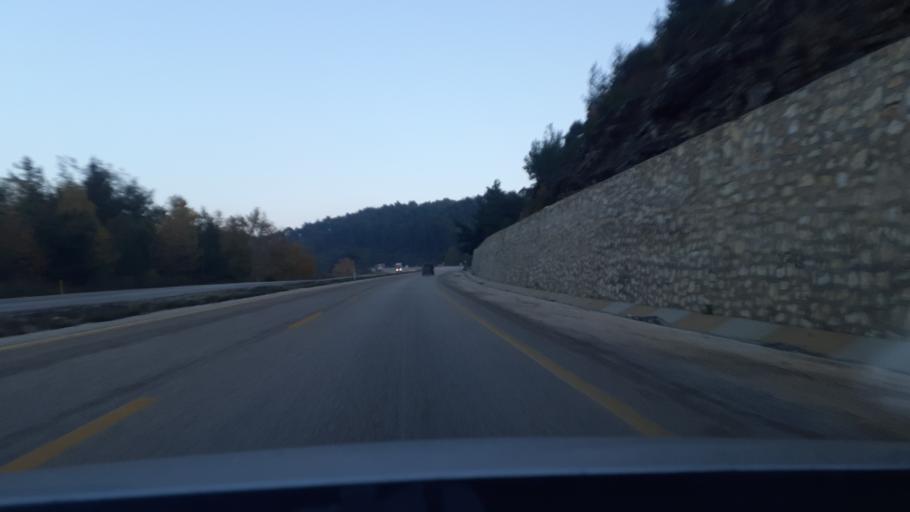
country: TR
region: Hatay
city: Yayladagi
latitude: 35.8931
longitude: 36.0845
